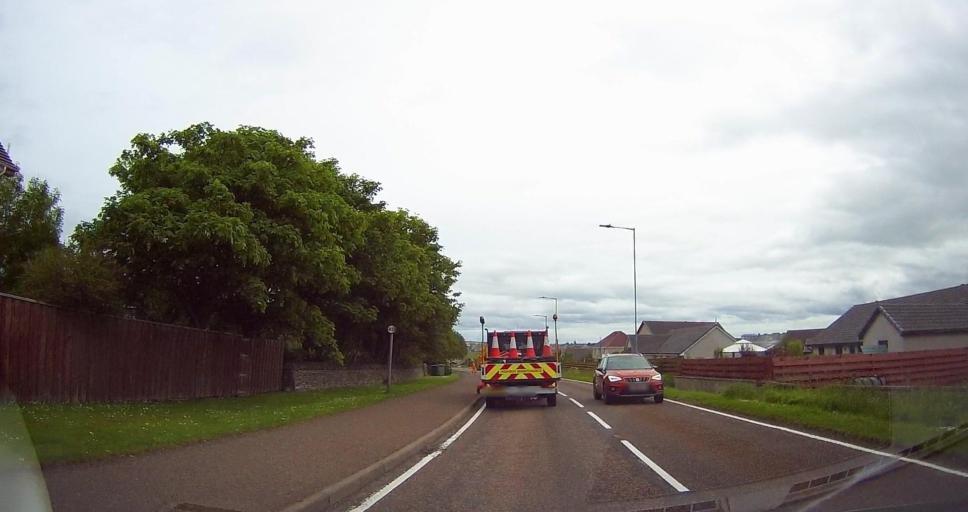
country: GB
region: Scotland
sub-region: Highland
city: Thurso
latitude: 58.6027
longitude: -3.5479
